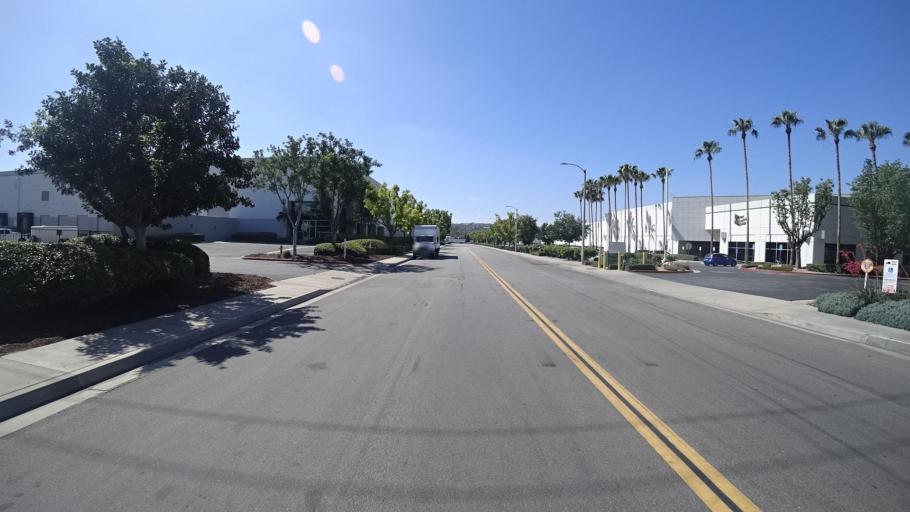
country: US
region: California
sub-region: Los Angeles County
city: Walnut
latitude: 34.0126
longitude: -117.8482
